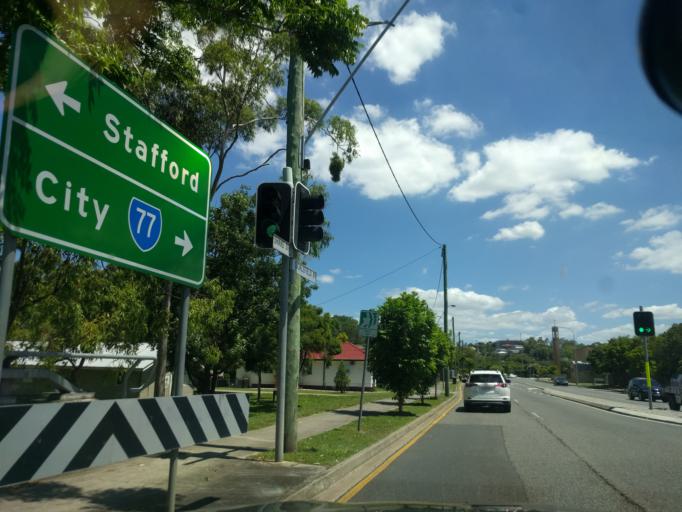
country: AU
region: Queensland
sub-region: Brisbane
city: Stafford
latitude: -27.4183
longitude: 152.9998
